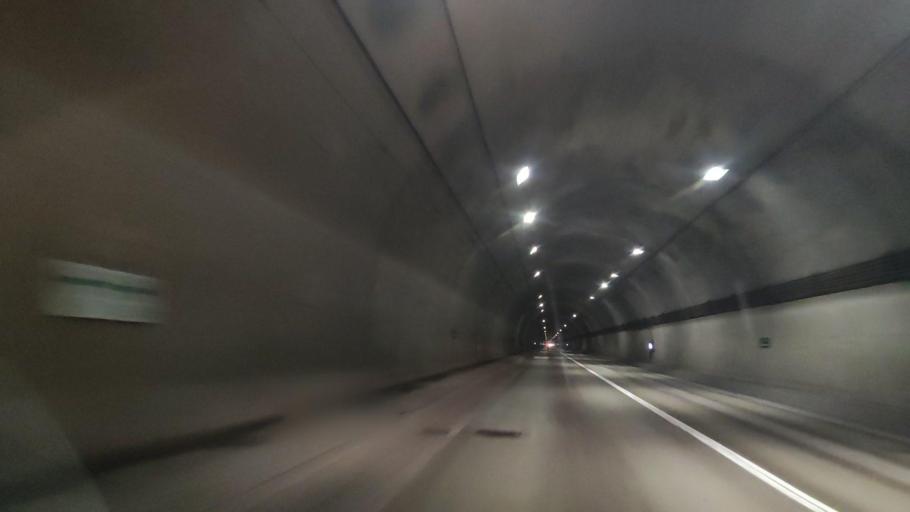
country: JP
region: Hokkaido
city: Niseko Town
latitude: 42.6002
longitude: 140.5551
